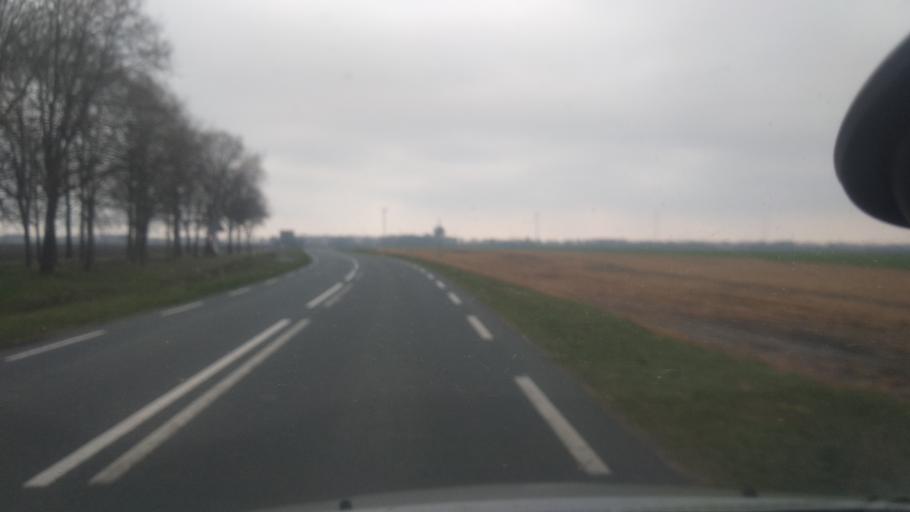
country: NL
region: Groningen
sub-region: Gemeente Stadskanaal
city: Stadskanaal
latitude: 52.9276
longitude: 6.9347
